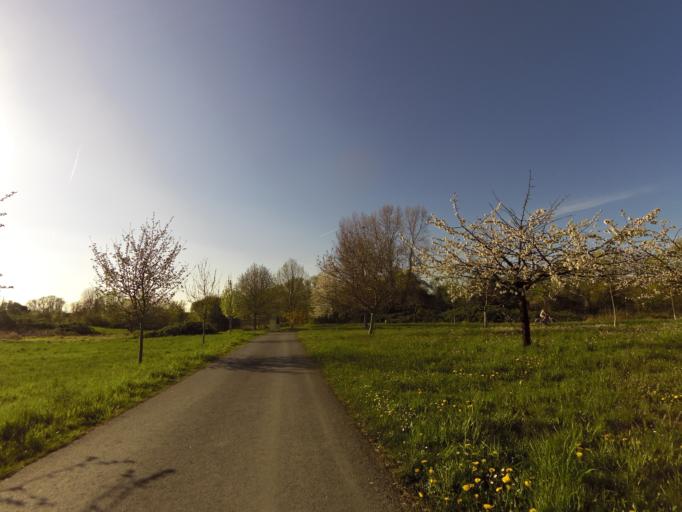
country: DE
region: Rheinland-Pfalz
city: Weitersburg
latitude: 50.4032
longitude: 7.5886
